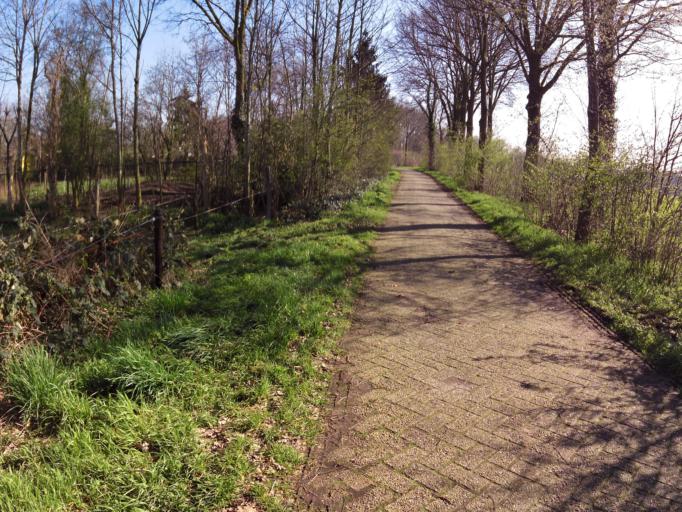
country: NL
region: North Brabant
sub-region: Gemeente Schijndel
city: Schijndel
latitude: 51.6694
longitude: 5.4084
